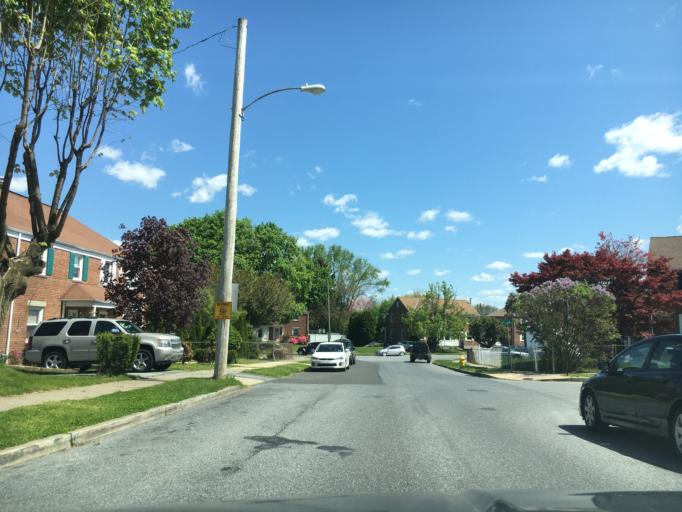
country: US
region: Pennsylvania
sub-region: Lehigh County
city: Allentown
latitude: 40.5799
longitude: -75.4825
